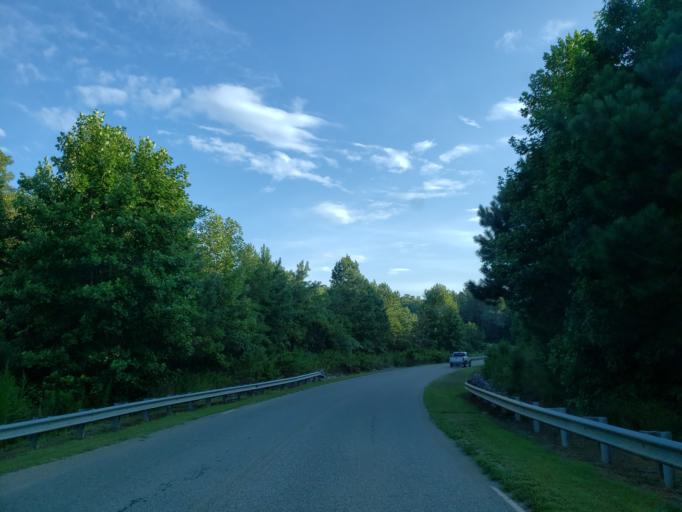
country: US
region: Georgia
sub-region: Cherokee County
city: Canton
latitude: 34.2279
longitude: -84.5729
